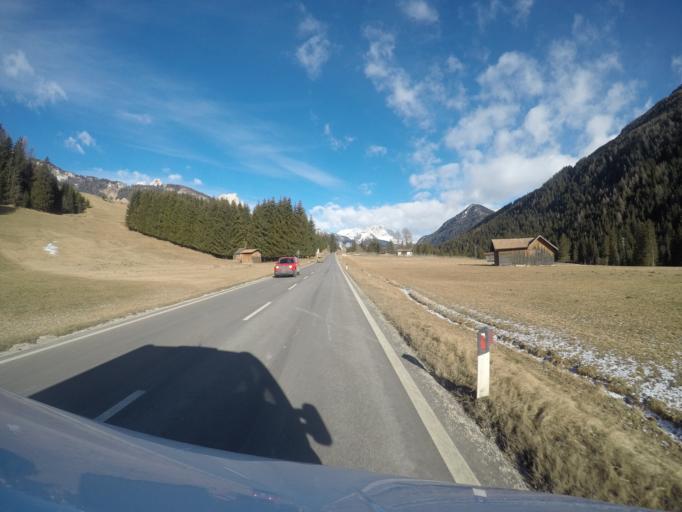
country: IT
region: Trentino-Alto Adige
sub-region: Provincia di Trento
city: Vigo di Fassa
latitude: 46.4111
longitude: 11.6772
